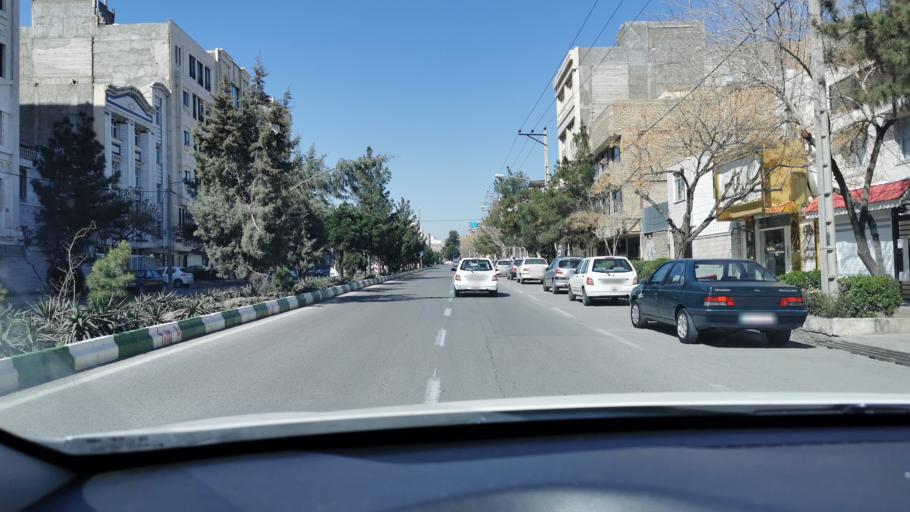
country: IR
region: Razavi Khorasan
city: Mashhad
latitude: 36.3261
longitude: 59.5213
